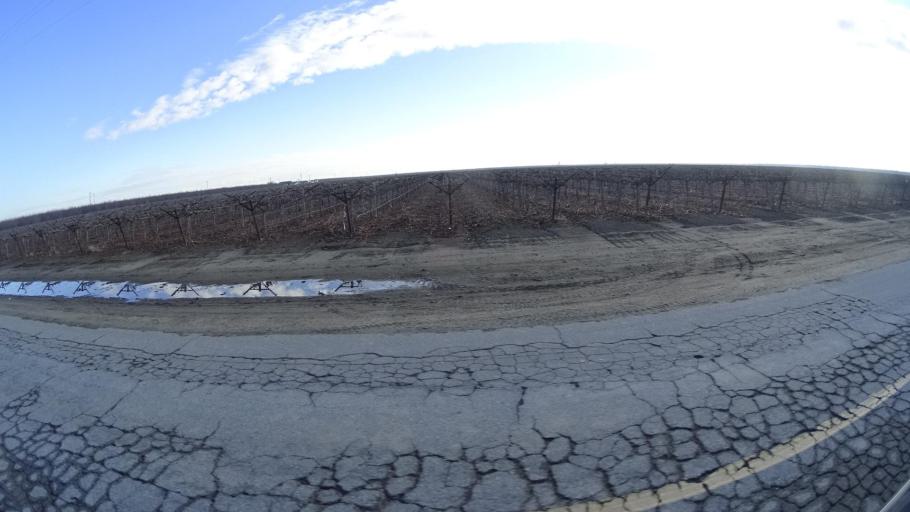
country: US
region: California
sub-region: Kern County
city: Delano
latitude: 35.7383
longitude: -119.3301
